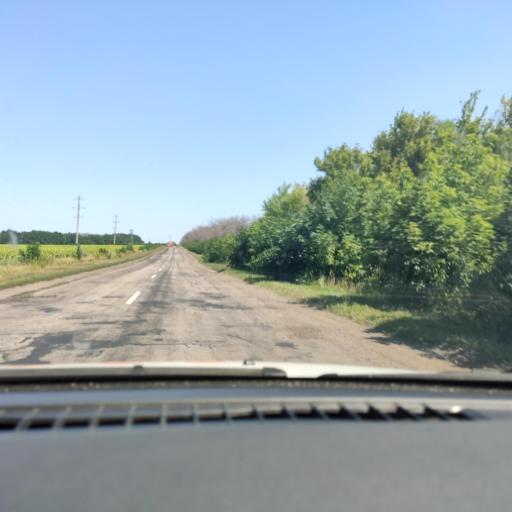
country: RU
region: Voronezj
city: Ol'khovatka
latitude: 50.6008
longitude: 39.3032
